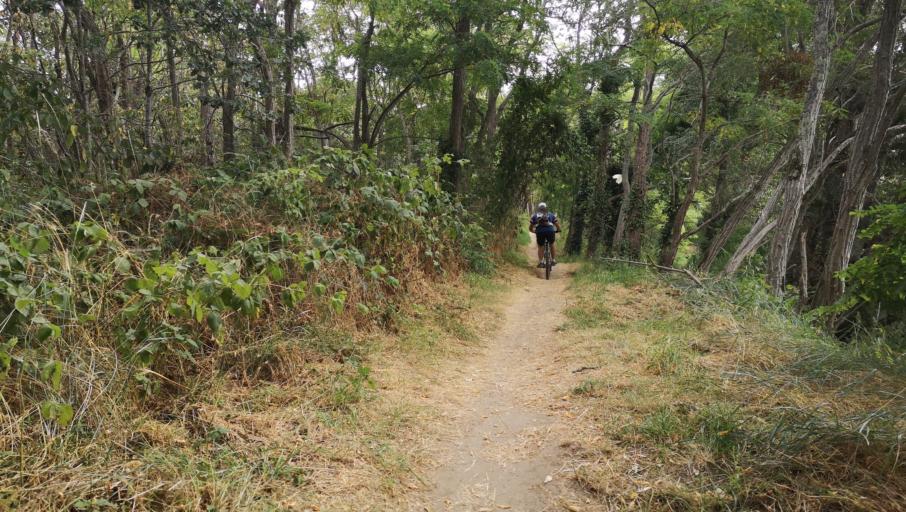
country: FR
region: Centre
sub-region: Departement du Loiret
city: Sandillon
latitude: 47.8606
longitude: 2.0494
